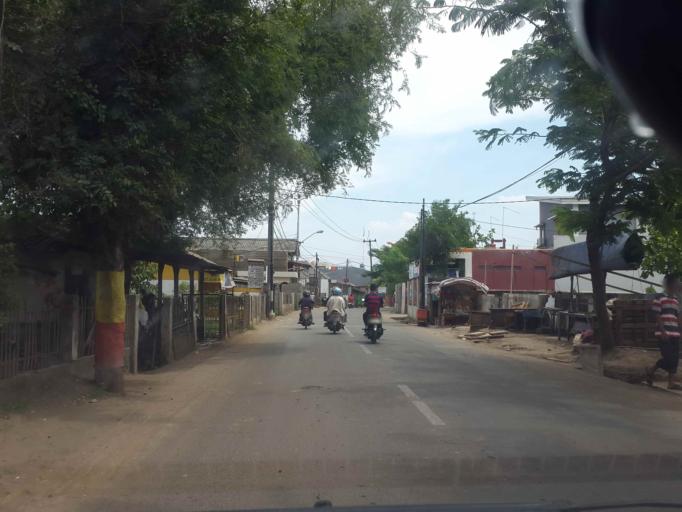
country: ID
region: Banten
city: Tangerang
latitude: -6.1538
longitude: 106.6264
